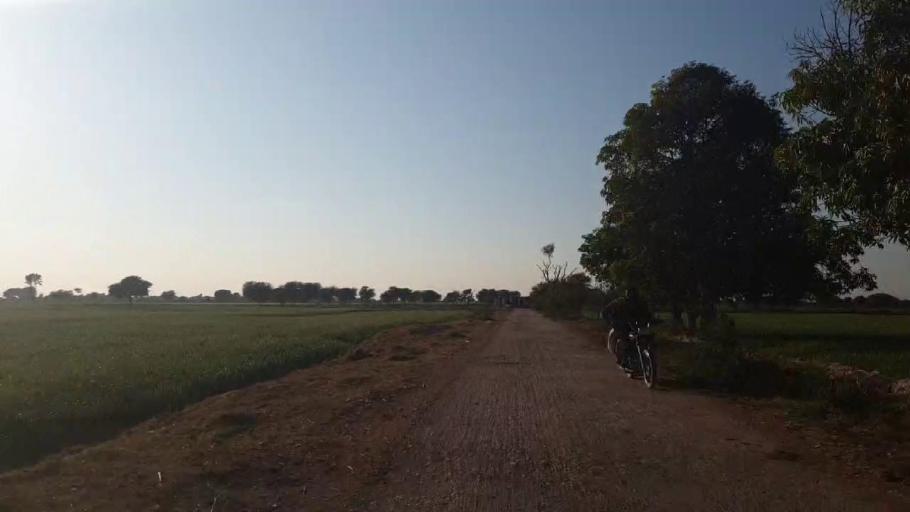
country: PK
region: Sindh
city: Shahpur Chakar
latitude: 26.0609
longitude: 68.6577
